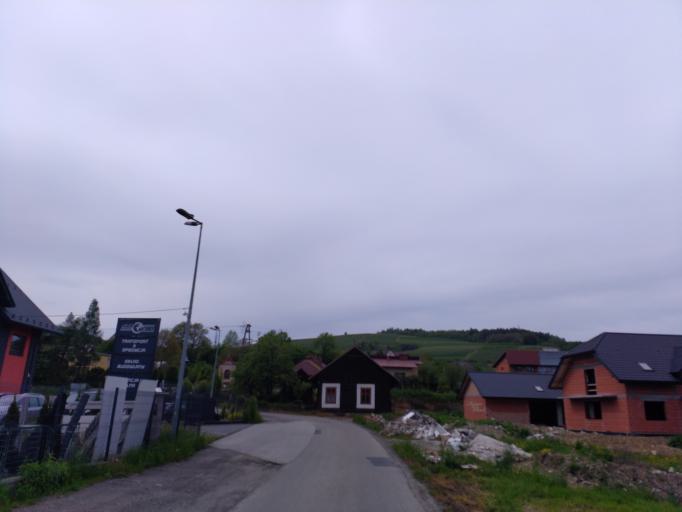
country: PL
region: Lesser Poland Voivodeship
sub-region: Powiat nowosadecki
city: Lacko
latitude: 49.5532
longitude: 20.4285
